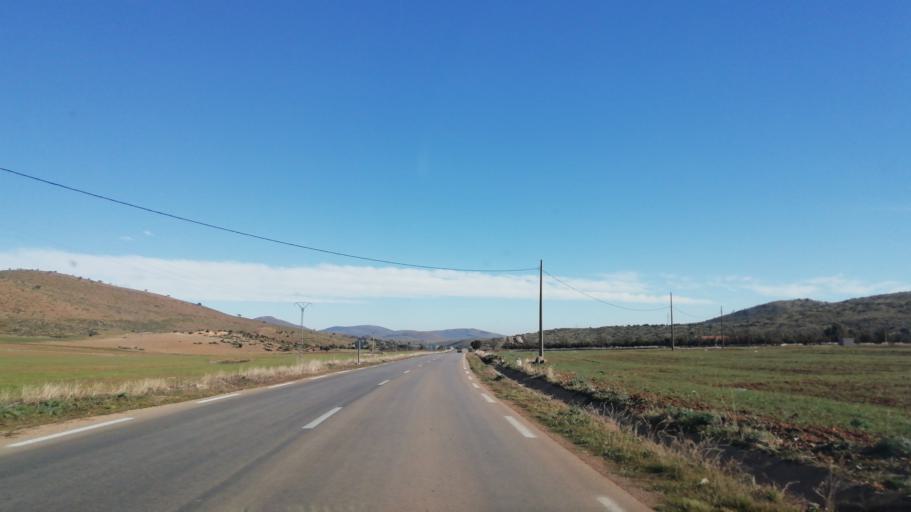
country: DZ
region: Tlemcen
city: Sebdou
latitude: 34.7449
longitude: -1.1648
